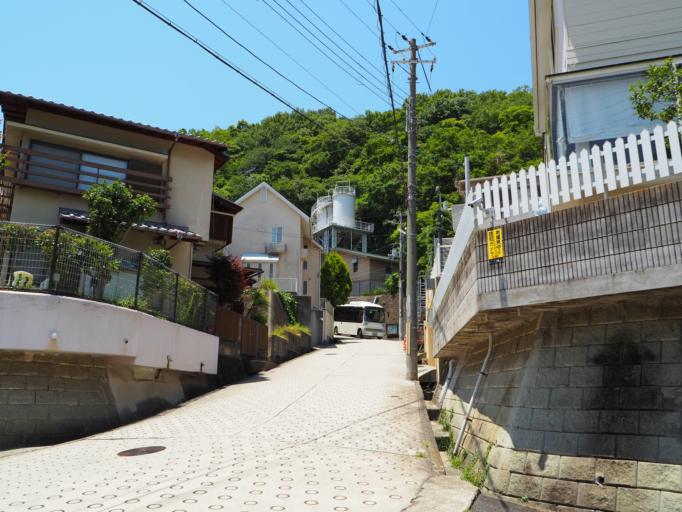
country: JP
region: Hyogo
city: Ashiya
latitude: 34.7403
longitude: 135.2900
